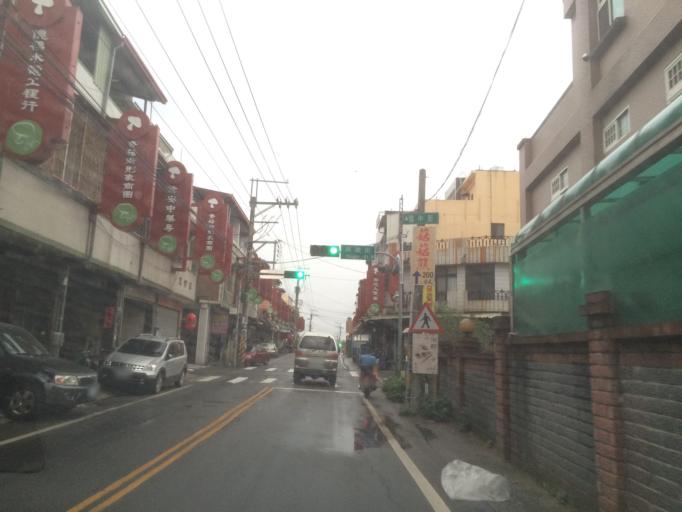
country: TW
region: Taiwan
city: Fengyuan
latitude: 24.1903
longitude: 120.8116
